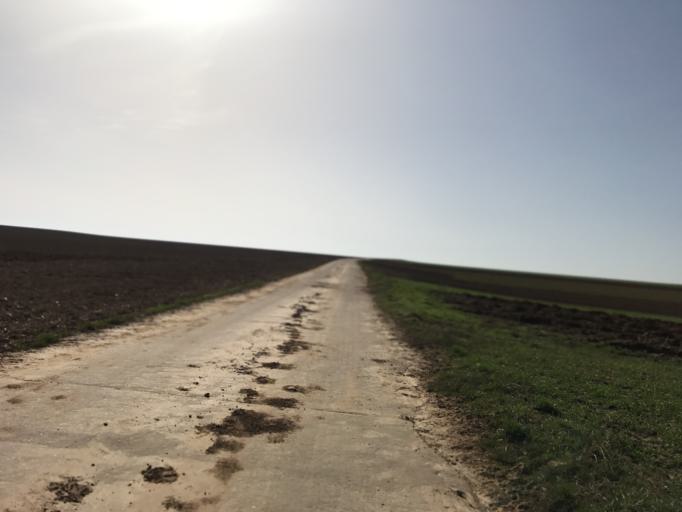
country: DE
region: Rheinland-Pfalz
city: Essenheim
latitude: 49.9369
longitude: 8.1406
